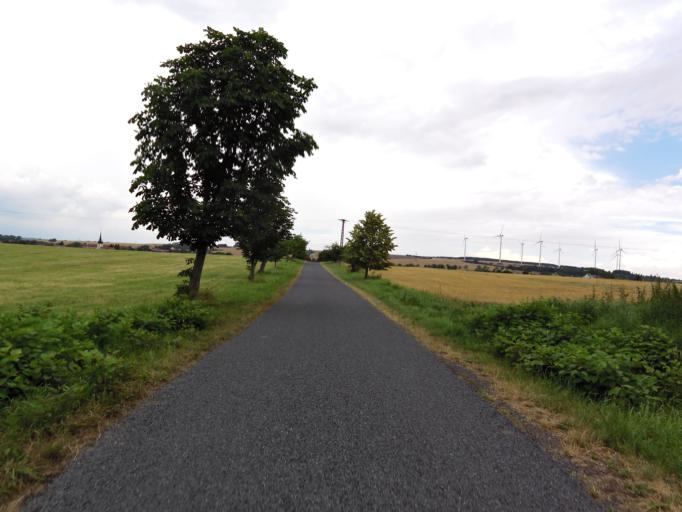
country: DE
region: Thuringia
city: Mechterstadt
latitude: 50.9348
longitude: 10.5265
